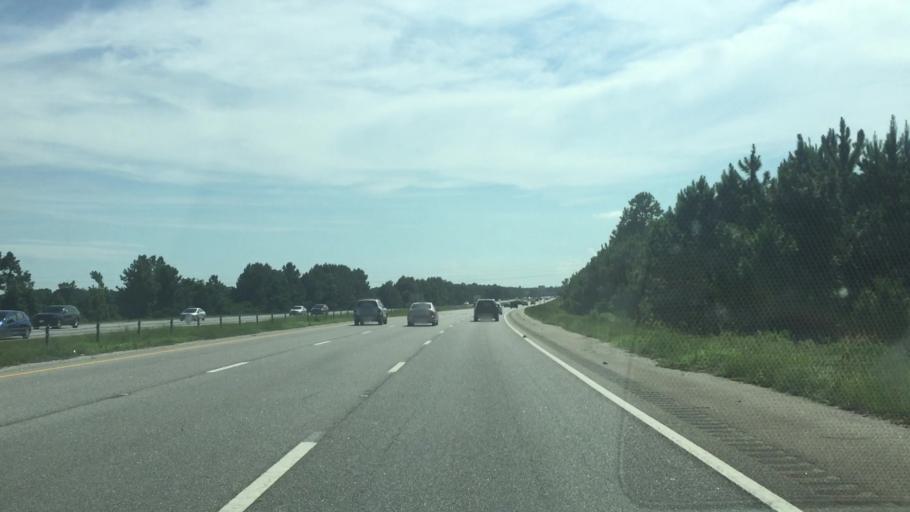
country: US
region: South Carolina
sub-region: Horry County
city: North Myrtle Beach
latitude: 33.8377
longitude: -78.7074
